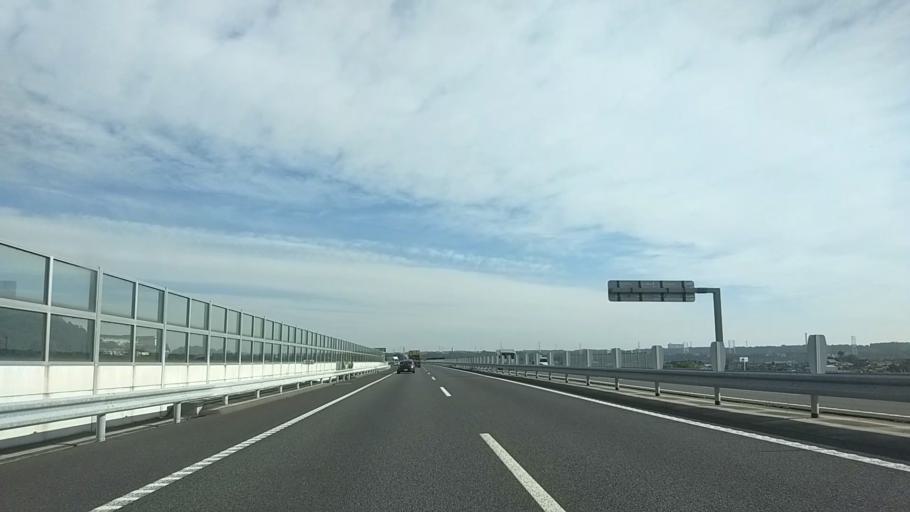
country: JP
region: Kanagawa
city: Zama
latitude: 35.5032
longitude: 139.3654
